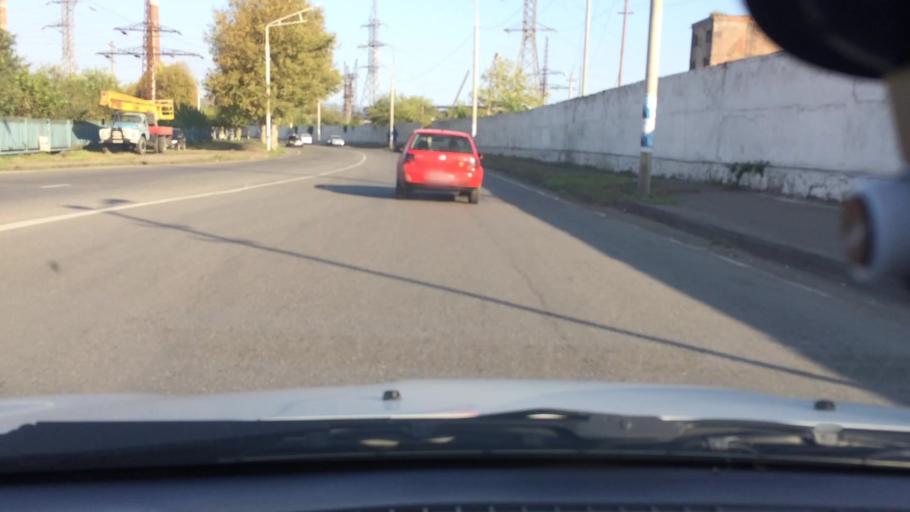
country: GE
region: Imereti
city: Zestap'oni
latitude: 42.1138
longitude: 43.0241
